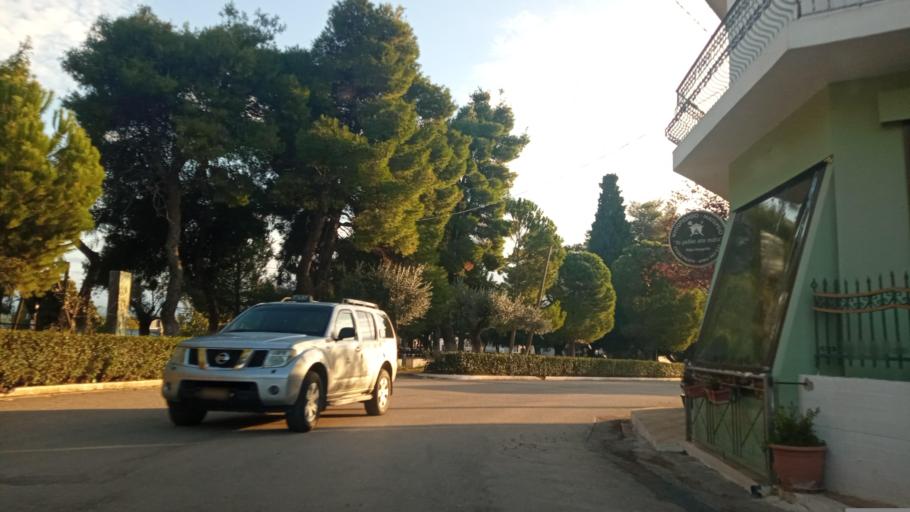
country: GR
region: Central Greece
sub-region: Nomos Evvoias
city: Psachna
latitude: 38.5818
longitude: 23.7133
